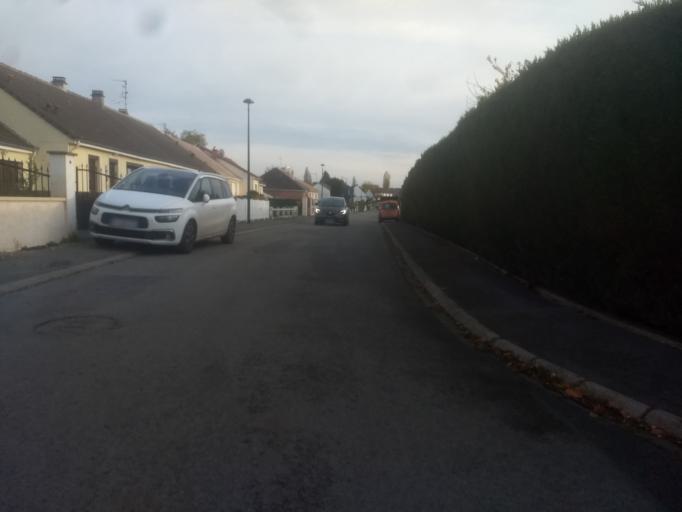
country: FR
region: Nord-Pas-de-Calais
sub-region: Departement du Pas-de-Calais
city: Beaurains
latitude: 50.2707
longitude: 2.7777
